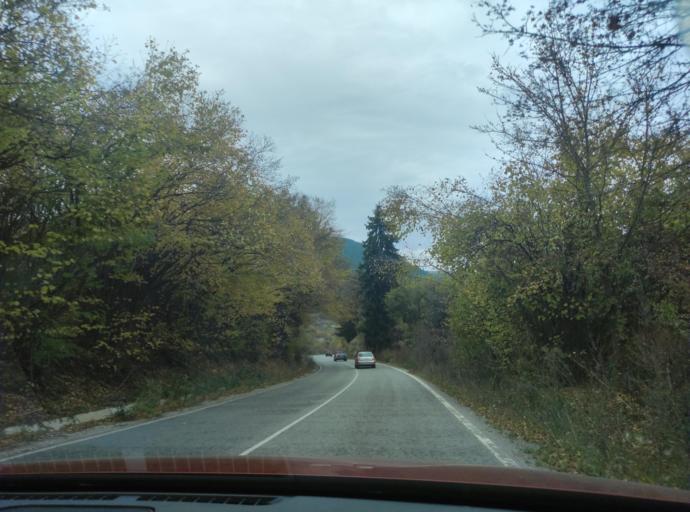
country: BG
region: Sofiya
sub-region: Obshtina Godech
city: Godech
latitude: 43.0304
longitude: 23.1361
